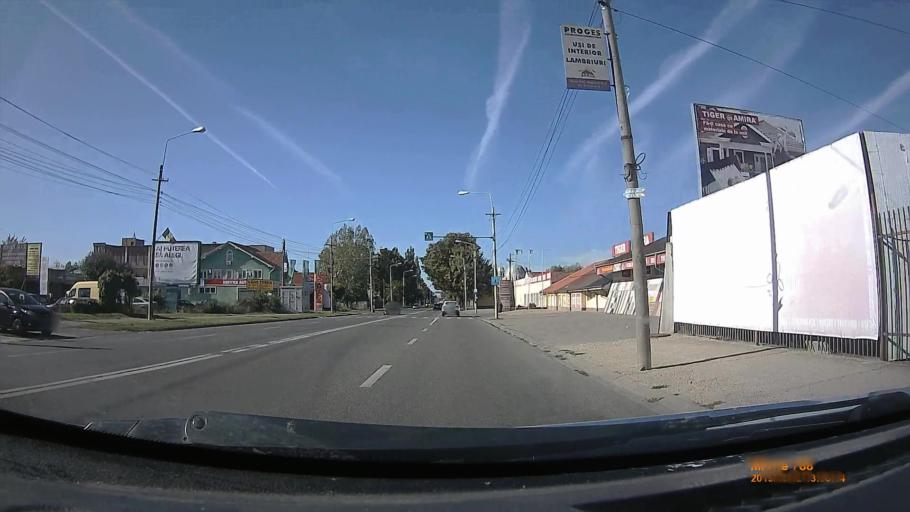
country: RO
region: Bihor
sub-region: Comuna Sanmartin
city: Sanmartin
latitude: 47.0393
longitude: 21.9797
